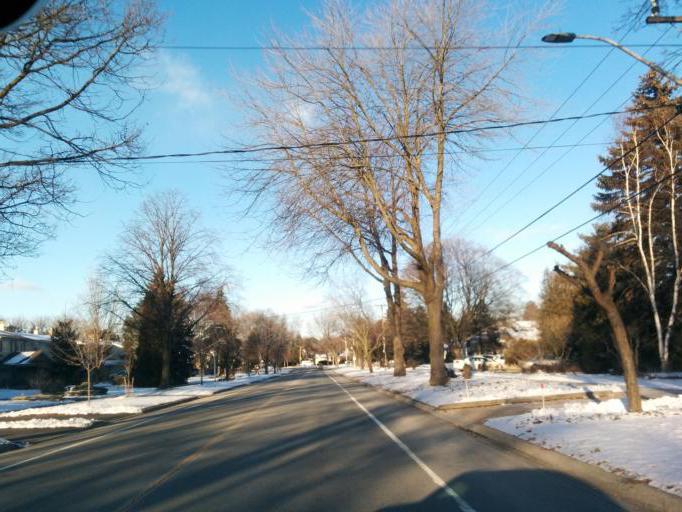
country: CA
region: Ontario
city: Mississauga
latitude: 43.5237
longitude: -79.6382
